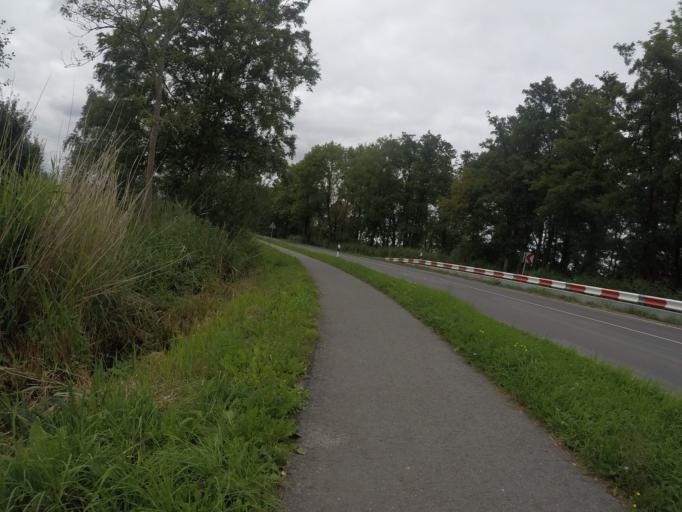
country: DE
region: Lower Saxony
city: Grossenworden
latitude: 53.6704
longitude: 9.2972
